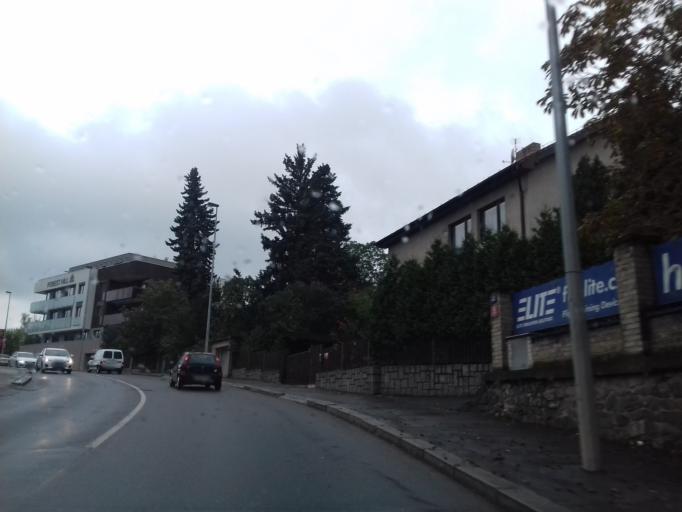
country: CZ
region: Praha
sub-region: Praha 1
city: Mala Strana
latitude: 50.0564
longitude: 14.3656
